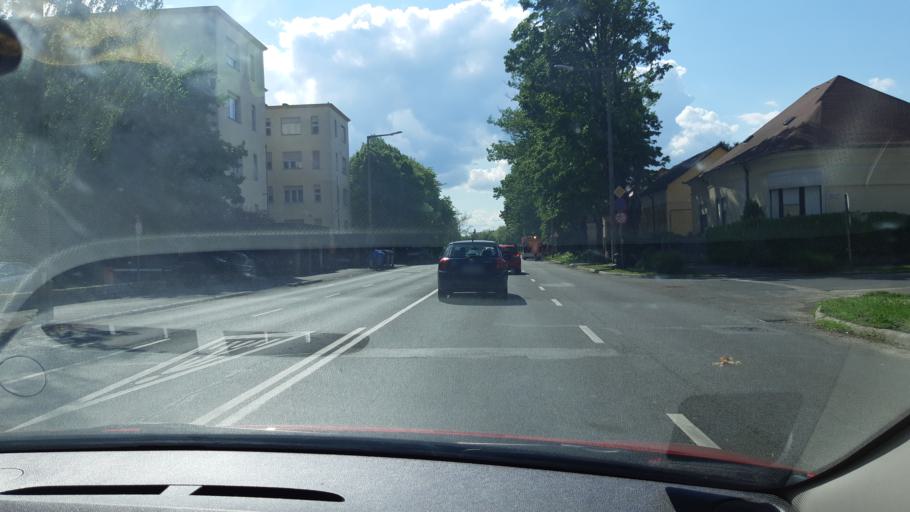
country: HU
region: Somogy
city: Kaposvar
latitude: 46.3651
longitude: 17.7931
